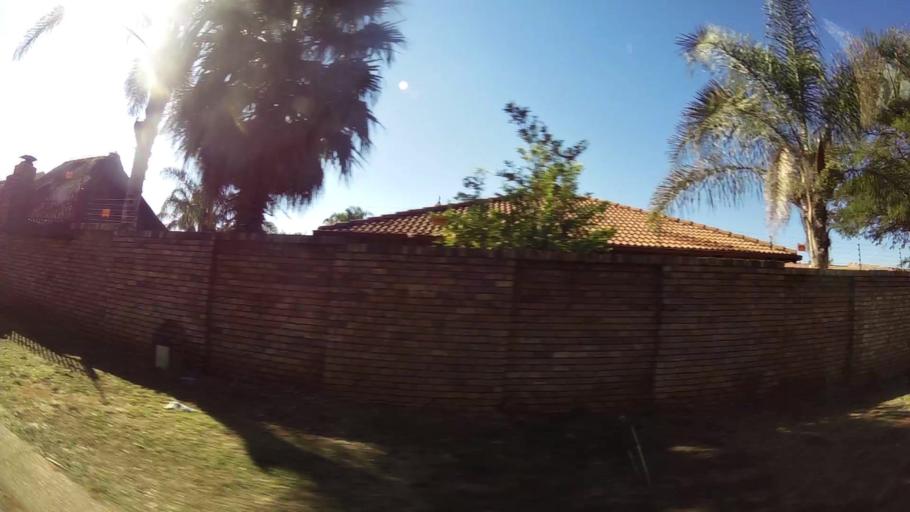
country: ZA
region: Gauteng
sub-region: City of Tshwane Metropolitan Municipality
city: Centurion
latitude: -25.8496
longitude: 28.2124
